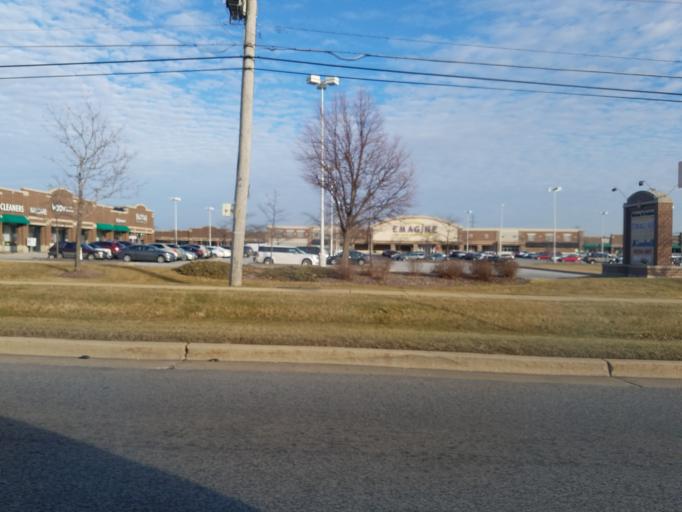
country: US
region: Illinois
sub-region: Will County
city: Frankfort
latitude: 41.5272
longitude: -87.8500
